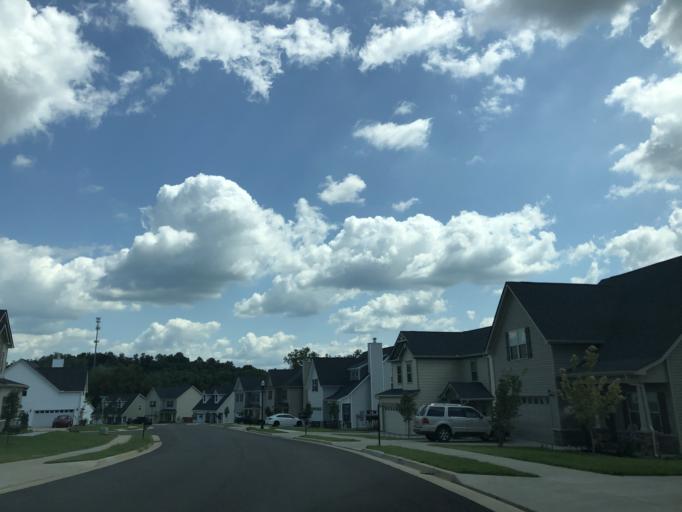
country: US
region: Tennessee
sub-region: Wilson County
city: Green Hill
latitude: 36.2119
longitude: -86.5832
